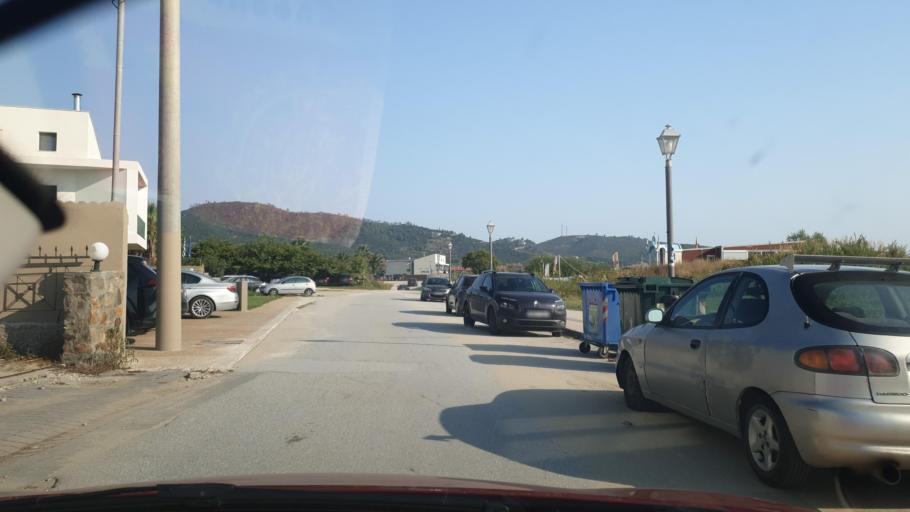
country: GR
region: Central Macedonia
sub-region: Nomos Chalkidikis
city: Sarti
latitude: 40.0845
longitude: 23.9787
